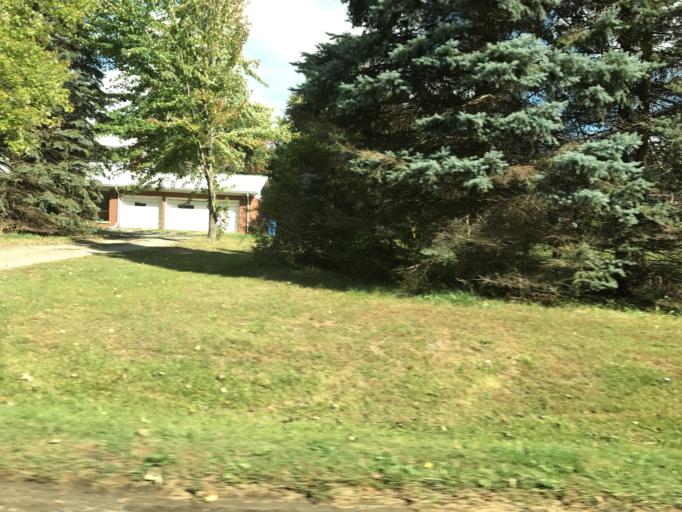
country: US
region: Michigan
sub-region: Oakland County
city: South Lyon
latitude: 42.4884
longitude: -83.6134
